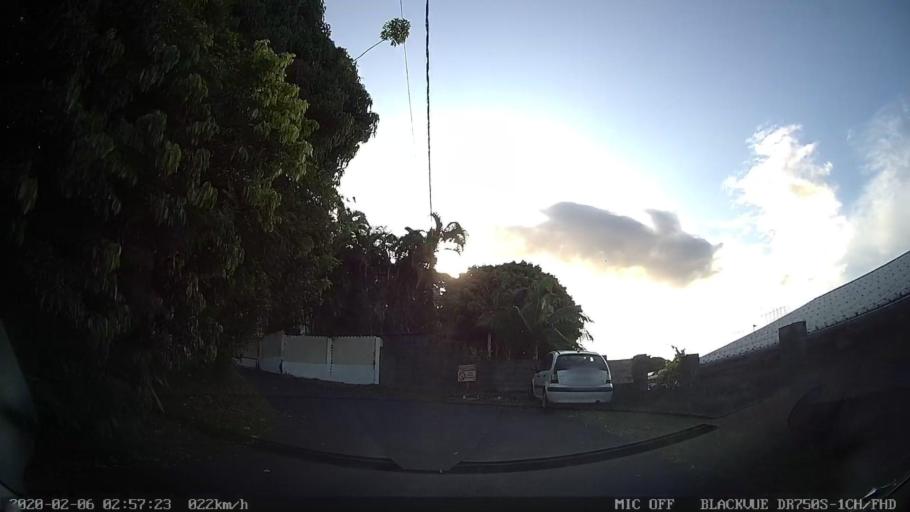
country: RE
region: Reunion
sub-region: Reunion
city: Sainte-Marie
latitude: -20.9353
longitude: 55.5295
